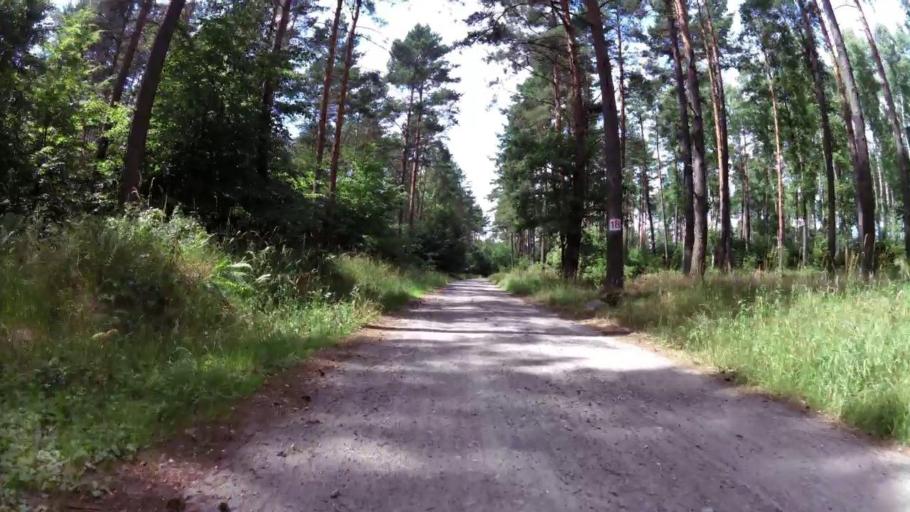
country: PL
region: West Pomeranian Voivodeship
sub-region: Powiat lobeski
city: Lobez
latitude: 53.5643
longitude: 15.6596
